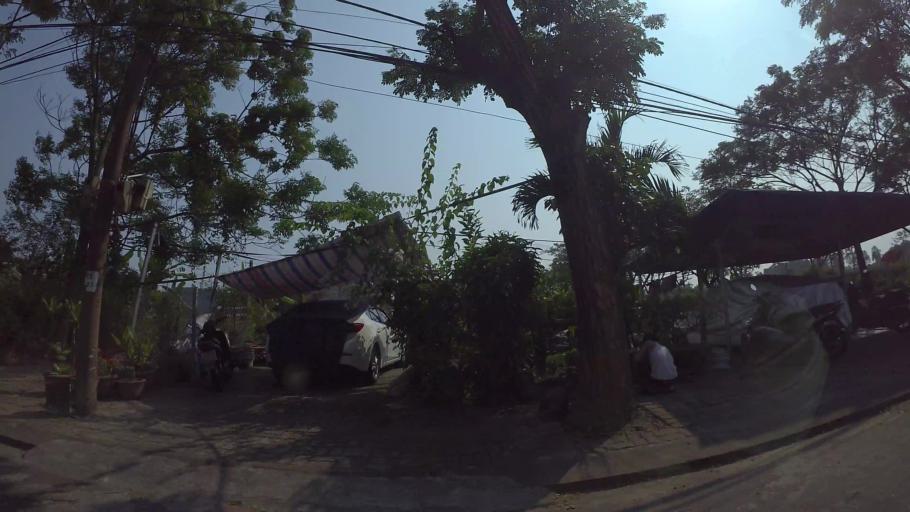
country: VN
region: Da Nang
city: Cam Le
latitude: 16.0081
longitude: 108.1928
